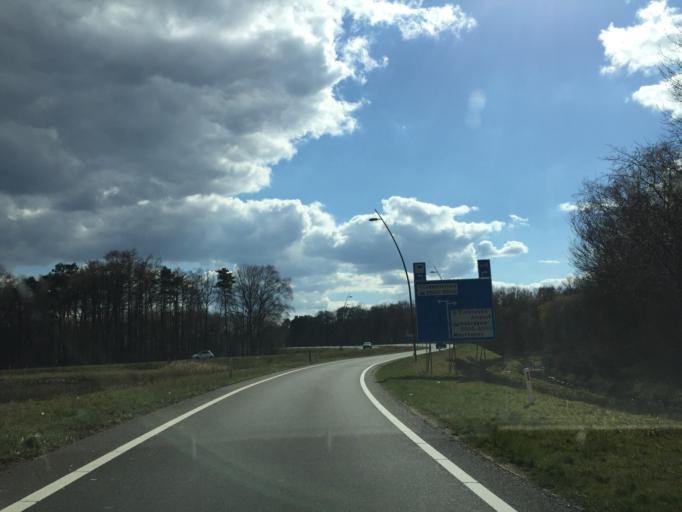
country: NL
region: North Brabant
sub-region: Gemeente Eindhoven
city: Meerhoven
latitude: 51.4619
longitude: 5.4067
